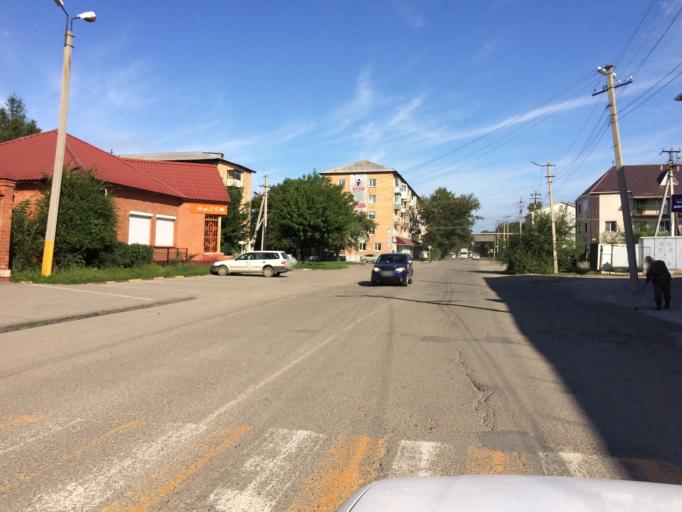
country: RU
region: Primorskiy
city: Dal'nerechensk
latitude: 45.9310
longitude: 133.7370
